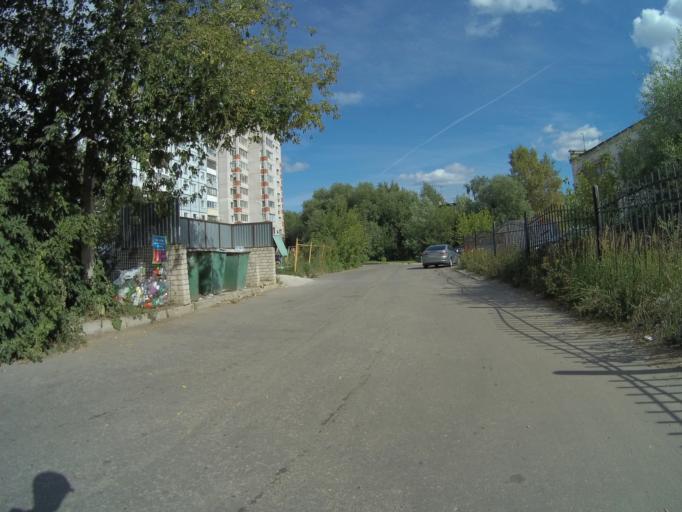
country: RU
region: Vladimir
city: Vladimir
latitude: 56.1371
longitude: 40.3668
